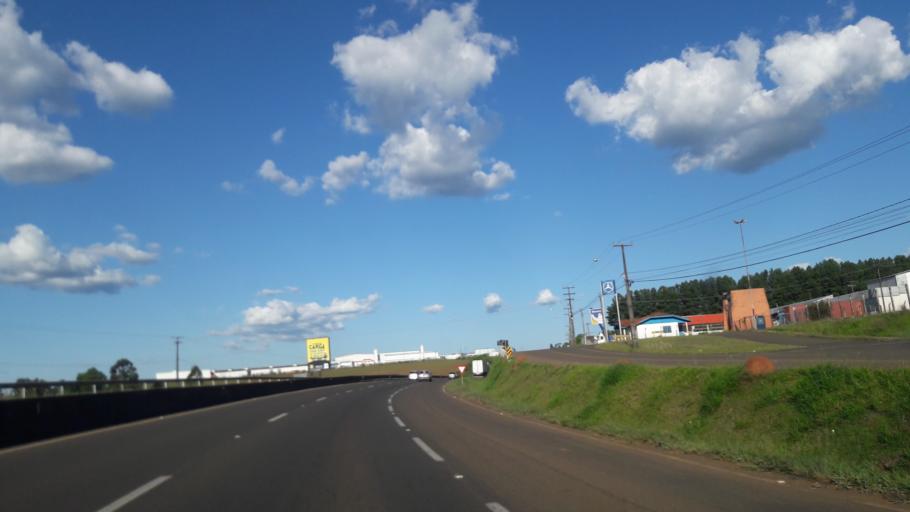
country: BR
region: Parana
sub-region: Guarapuava
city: Guarapuava
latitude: -25.3487
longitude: -51.4551
